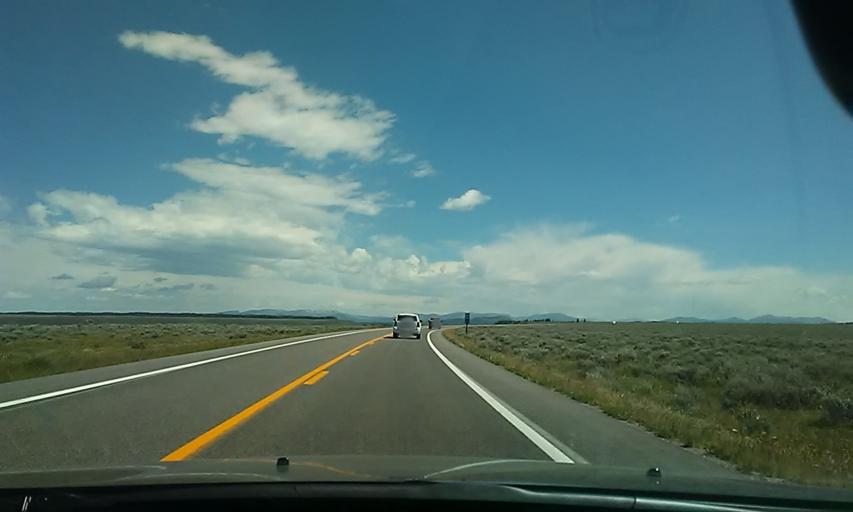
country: US
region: Wyoming
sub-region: Teton County
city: Jackson
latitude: 43.7201
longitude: -110.6587
